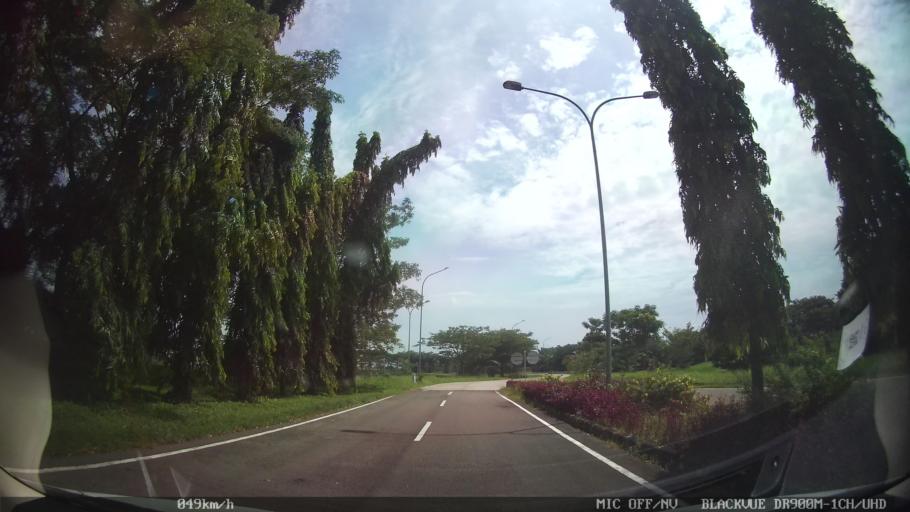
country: ID
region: North Sumatra
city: Percut
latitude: 3.6312
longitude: 98.8716
